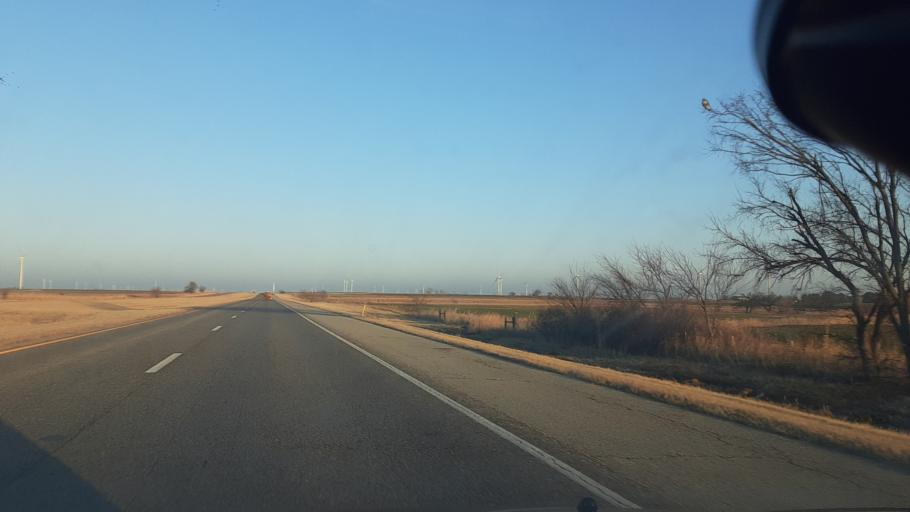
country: US
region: Oklahoma
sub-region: Noble County
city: Perry
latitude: 36.3975
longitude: -97.5051
